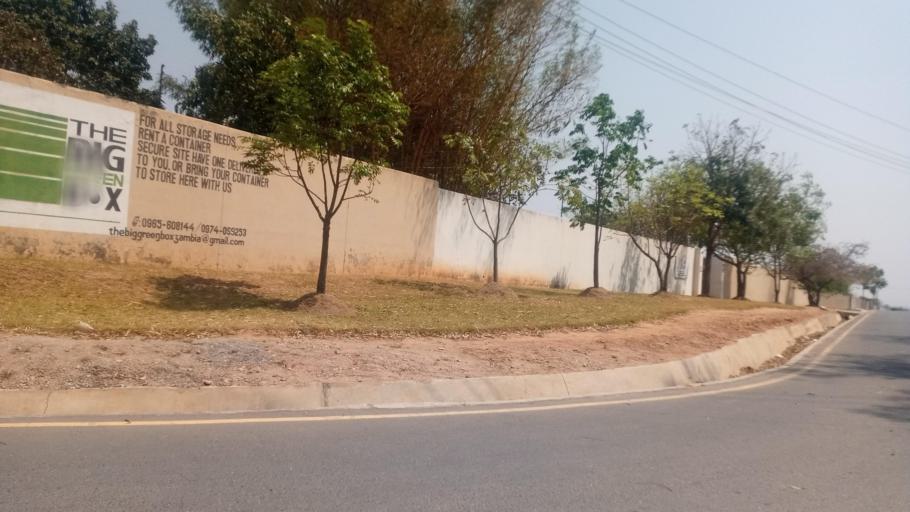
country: ZM
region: Lusaka
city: Lusaka
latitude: -15.4310
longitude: 28.3734
